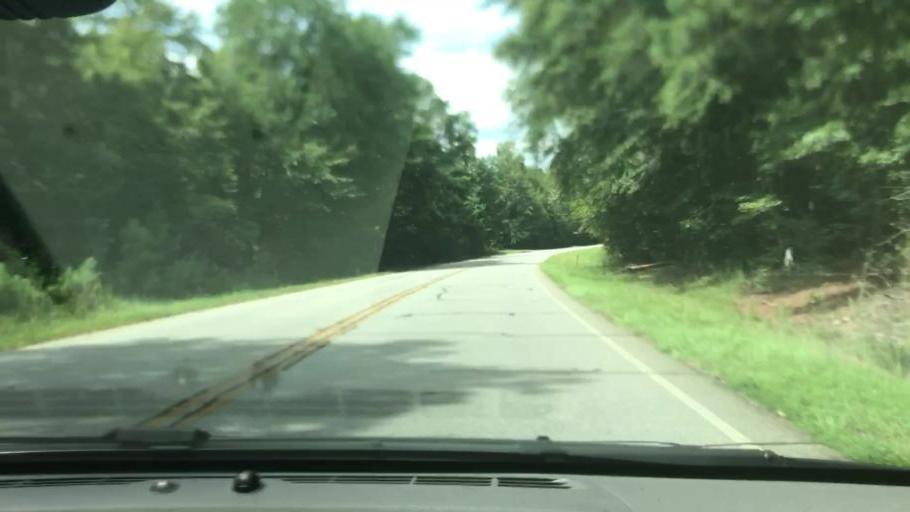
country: US
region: Georgia
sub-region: Stewart County
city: Lumpkin
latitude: 32.1462
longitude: -84.8934
